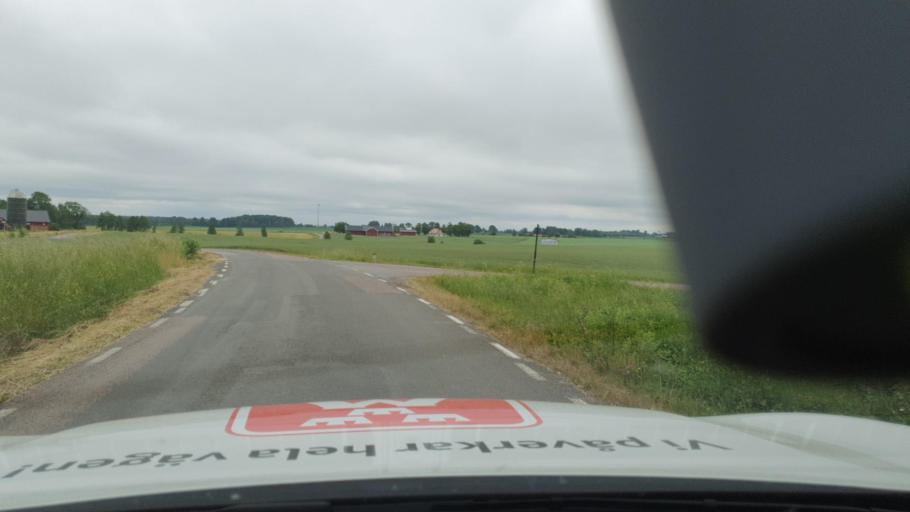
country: SE
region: Vaestra Goetaland
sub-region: Tibro Kommun
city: Tibro
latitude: 58.3600
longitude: 14.0789
